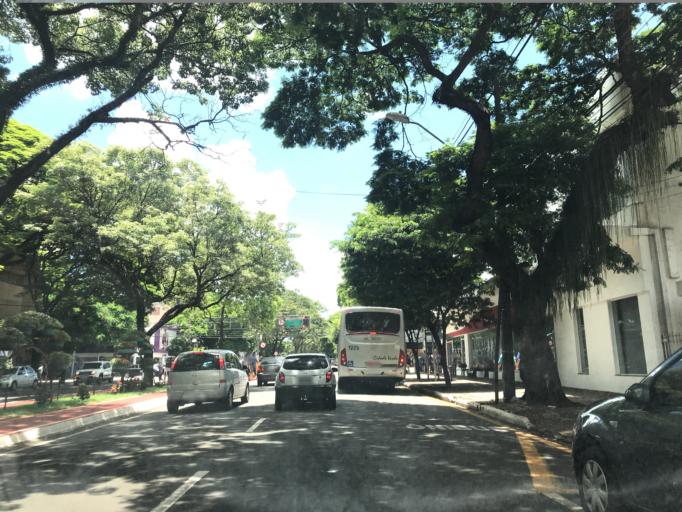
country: BR
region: Parana
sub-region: Maringa
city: Maringa
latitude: -23.4209
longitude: -51.9323
